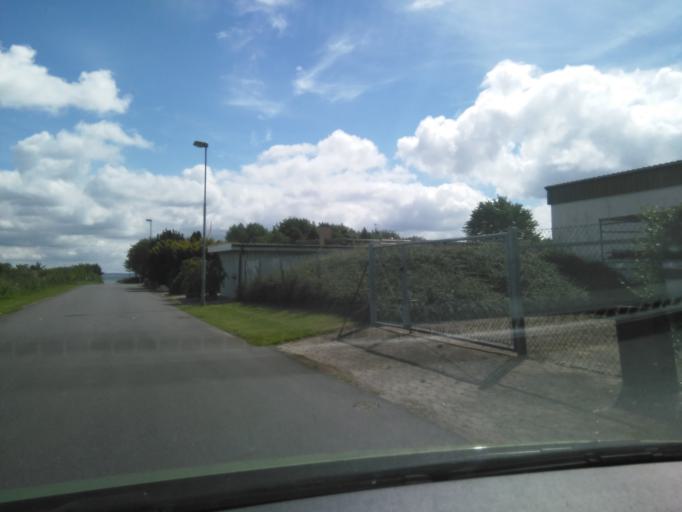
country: DK
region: Central Jutland
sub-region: Arhus Kommune
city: Logten
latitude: 56.2603
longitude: 10.3402
